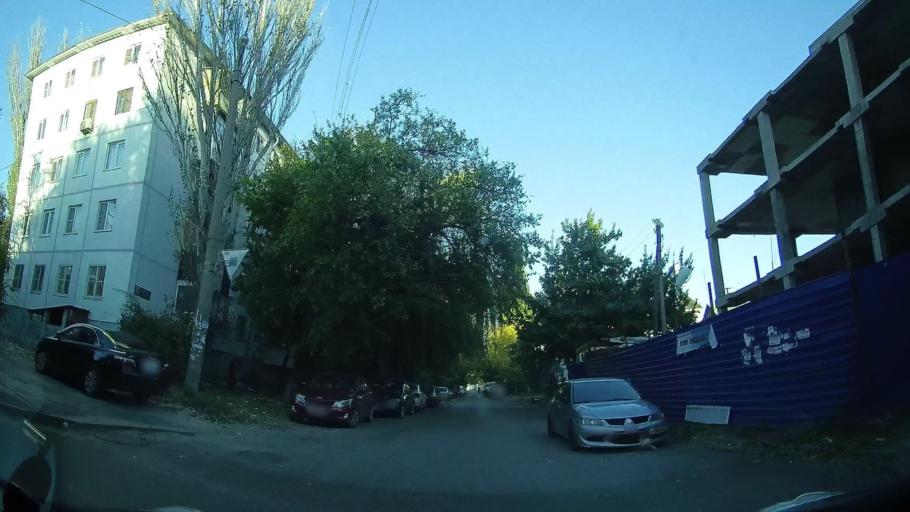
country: RU
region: Rostov
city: Rostov-na-Donu
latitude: 47.2332
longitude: 39.6937
